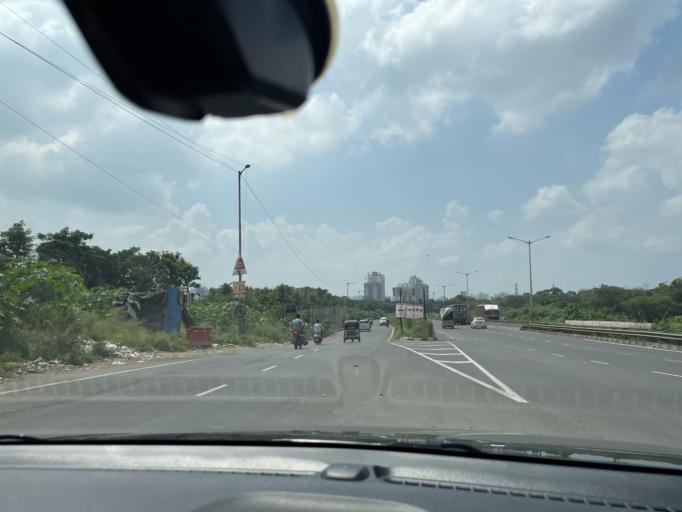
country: IN
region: Maharashtra
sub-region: Pune Division
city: Shivaji Nagar
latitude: 18.5320
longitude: 73.7799
